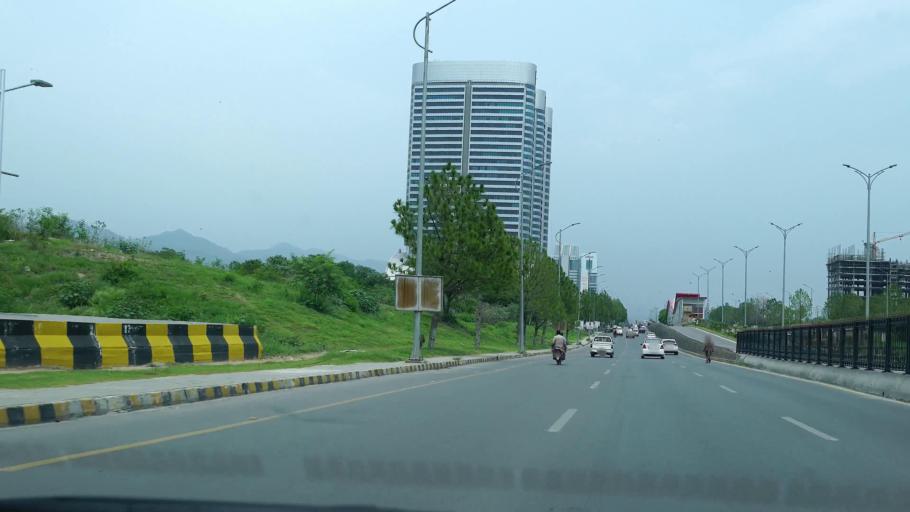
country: PK
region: Islamabad
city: Islamabad
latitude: 33.7015
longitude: 73.0398
